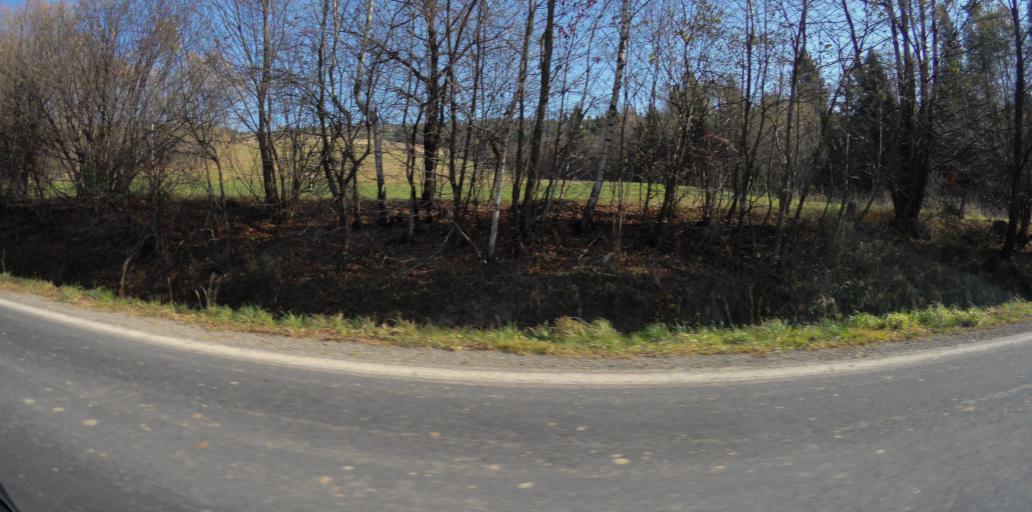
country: PL
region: Subcarpathian Voivodeship
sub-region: Powiat bieszczadzki
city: Ustrzyki Dolne
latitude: 49.5268
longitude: 22.6037
